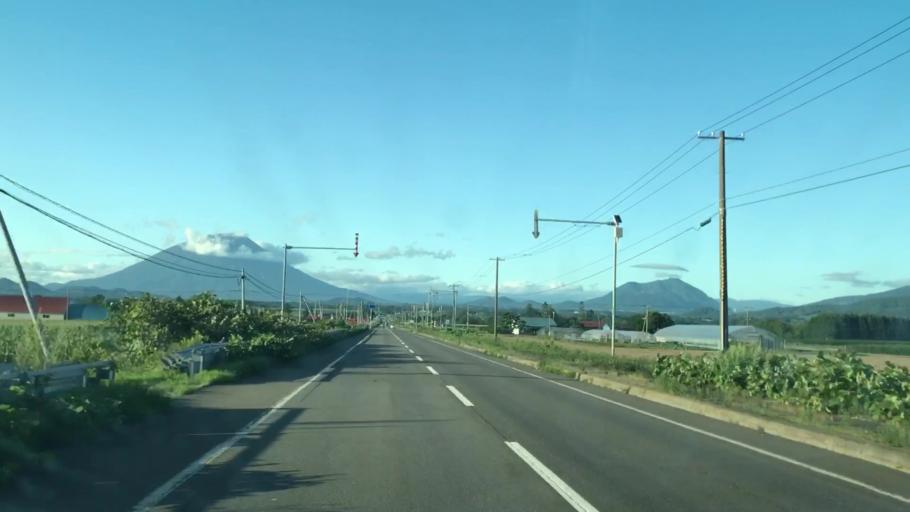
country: JP
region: Hokkaido
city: Date
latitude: 42.6317
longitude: 140.8004
